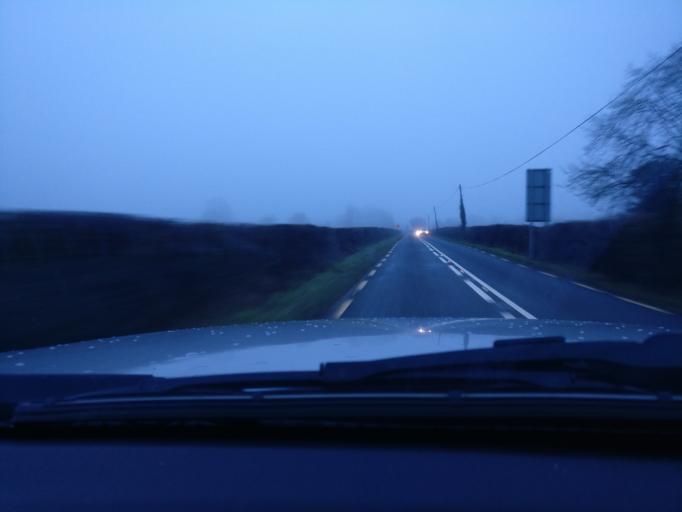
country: IE
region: Leinster
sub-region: An Mhi
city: Ballivor
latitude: 53.6049
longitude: -6.9923
